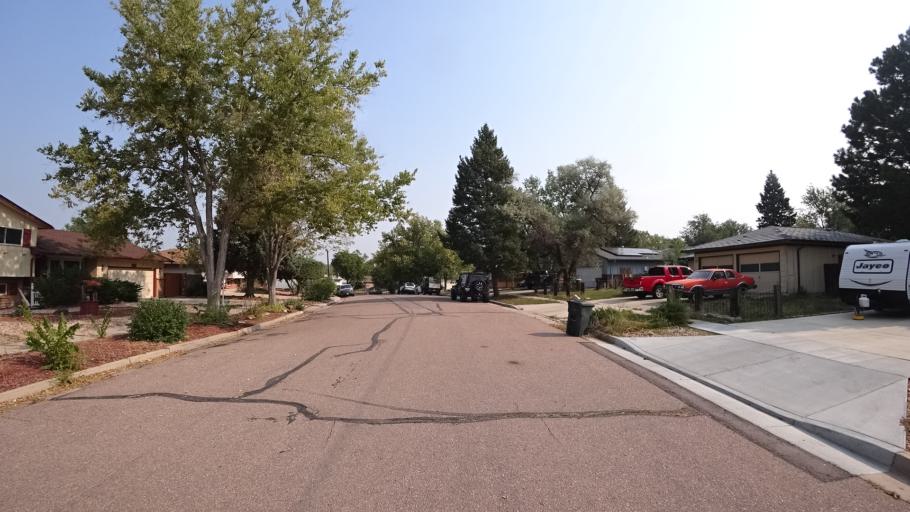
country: US
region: Colorado
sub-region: El Paso County
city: Stratmoor
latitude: 38.8160
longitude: -104.7756
